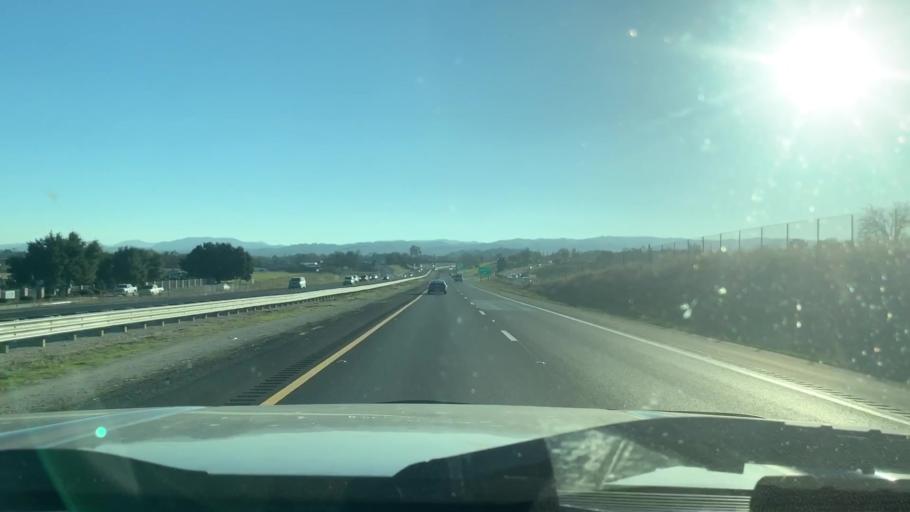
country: US
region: California
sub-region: San Luis Obispo County
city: Templeton
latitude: 35.5711
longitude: -120.6998
